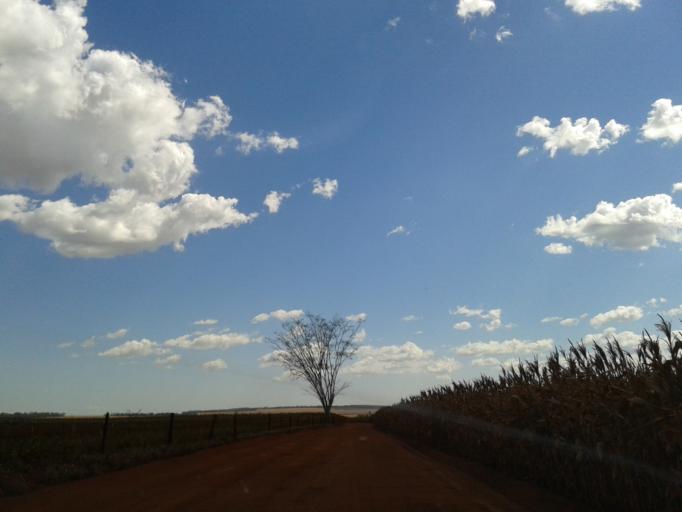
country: BR
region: Minas Gerais
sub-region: Capinopolis
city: Capinopolis
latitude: -18.5995
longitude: -49.5136
